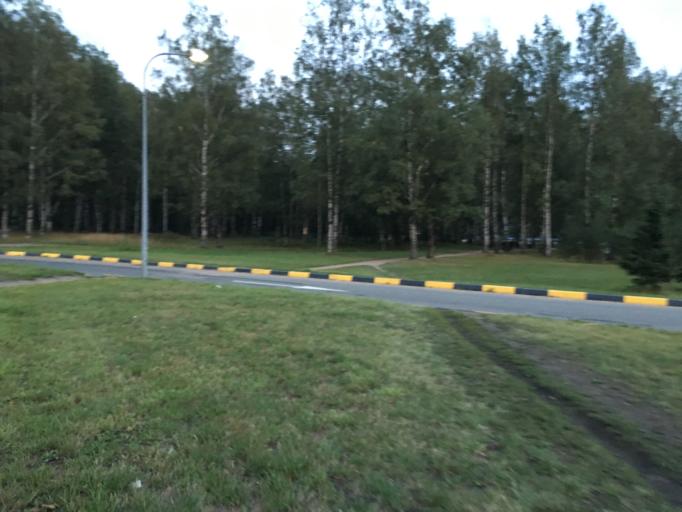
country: RU
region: Leningrad
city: Kalininskiy
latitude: 59.9942
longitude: 30.3926
